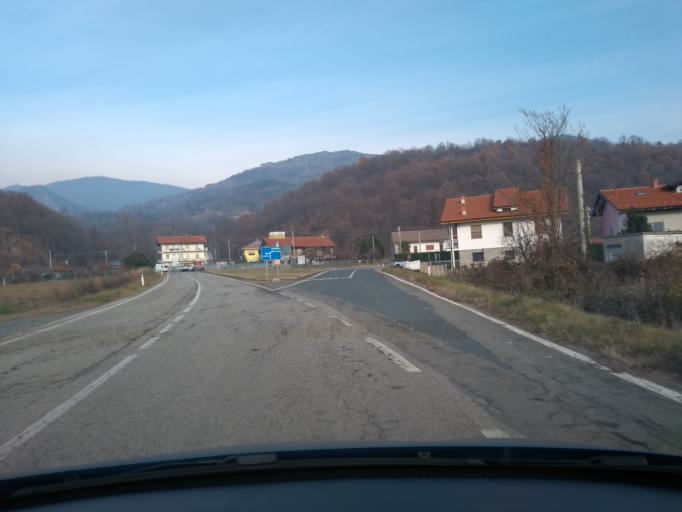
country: IT
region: Piedmont
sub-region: Provincia di Torino
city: Balangero
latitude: 45.2756
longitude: 7.5128
